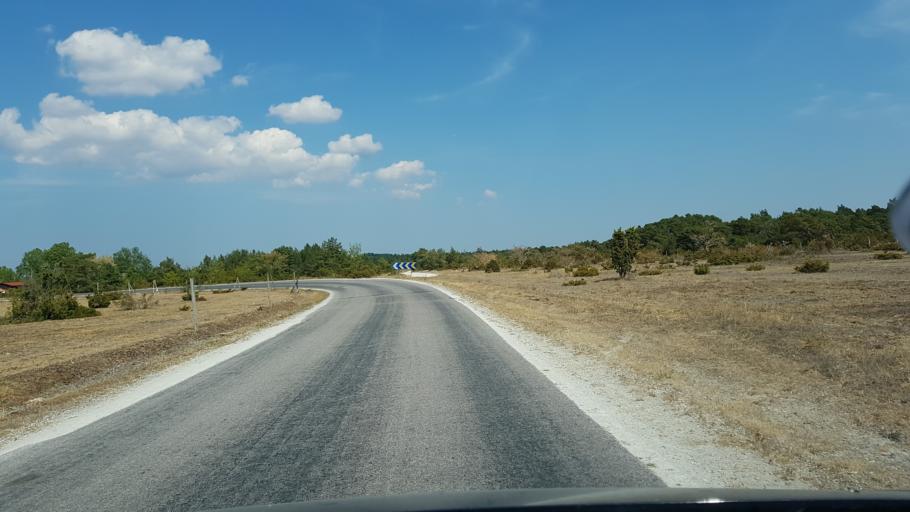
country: SE
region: Gotland
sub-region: Gotland
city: Visby
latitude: 57.6620
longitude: 18.3760
